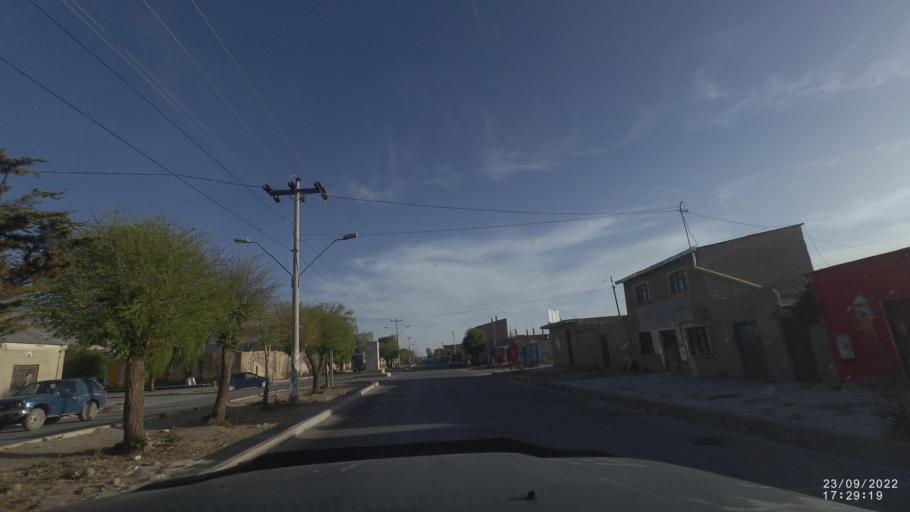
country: BO
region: Oruro
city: Challapata
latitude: -18.9019
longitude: -66.7770
